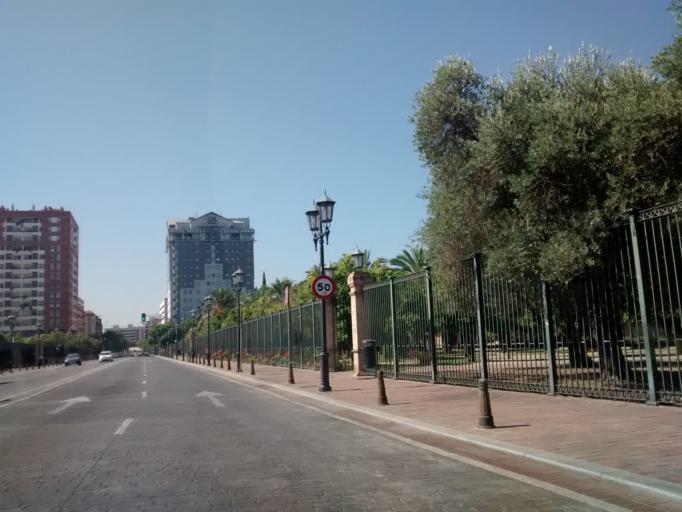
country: ES
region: Andalusia
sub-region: Provincia de Sevilla
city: Sevilla
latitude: 37.3838
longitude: -5.9796
